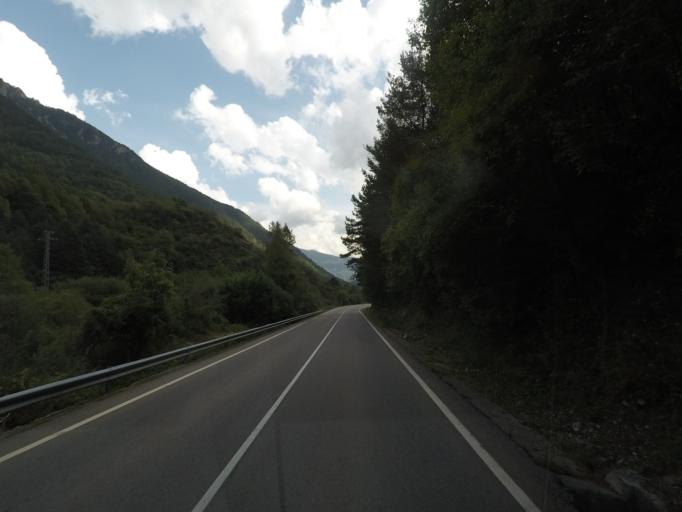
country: ES
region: Aragon
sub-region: Provincia de Huesca
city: Bielsa
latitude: 42.6515
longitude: 0.2086
